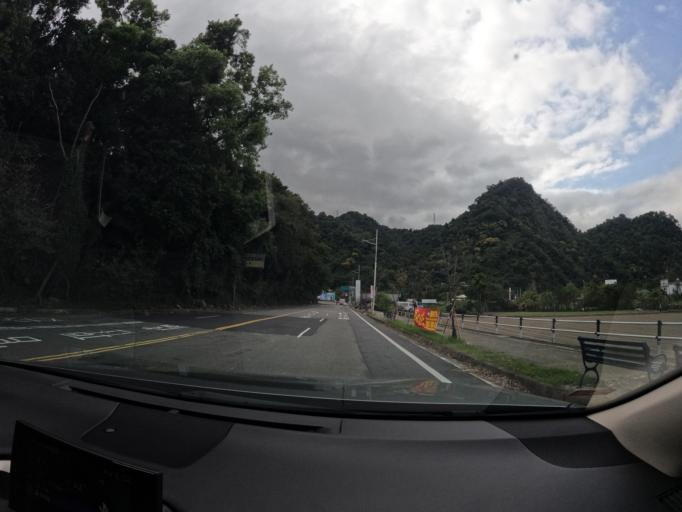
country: TW
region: Taiwan
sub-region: Miaoli
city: Miaoli
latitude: 24.4518
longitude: 120.8765
